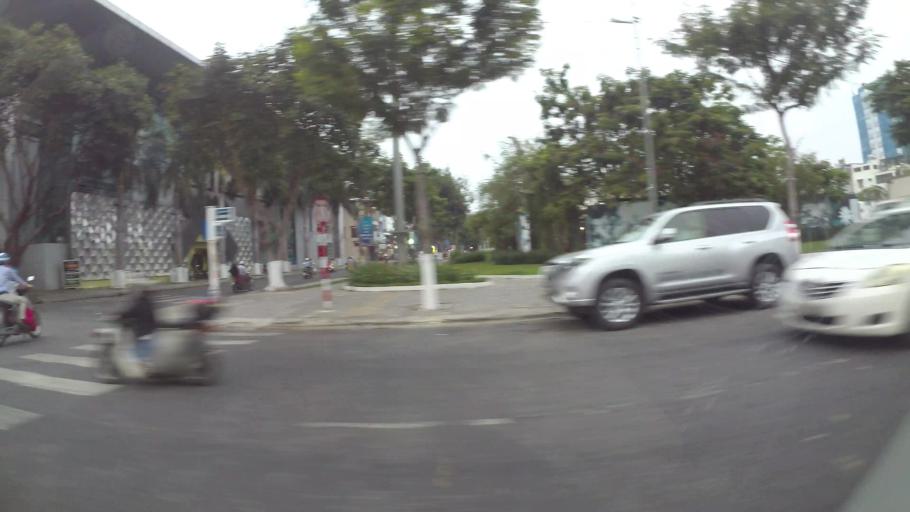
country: VN
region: Da Nang
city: Da Nang
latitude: 16.0686
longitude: 108.2212
